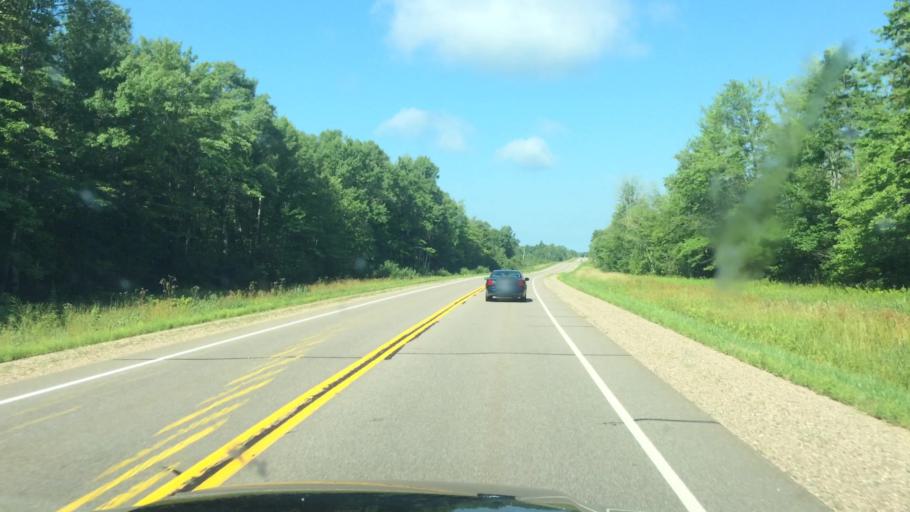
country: US
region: Wisconsin
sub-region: Langlade County
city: Antigo
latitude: 45.1440
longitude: -89.3000
